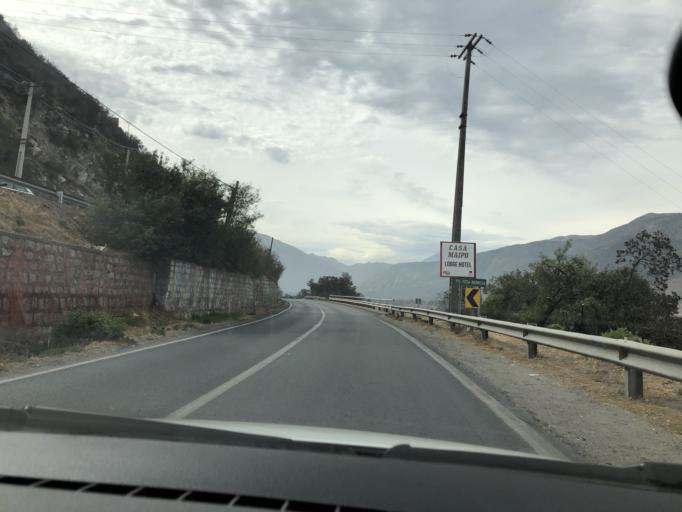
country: CL
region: Santiago Metropolitan
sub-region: Provincia de Cordillera
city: Puente Alto
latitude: -33.5979
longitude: -70.4956
